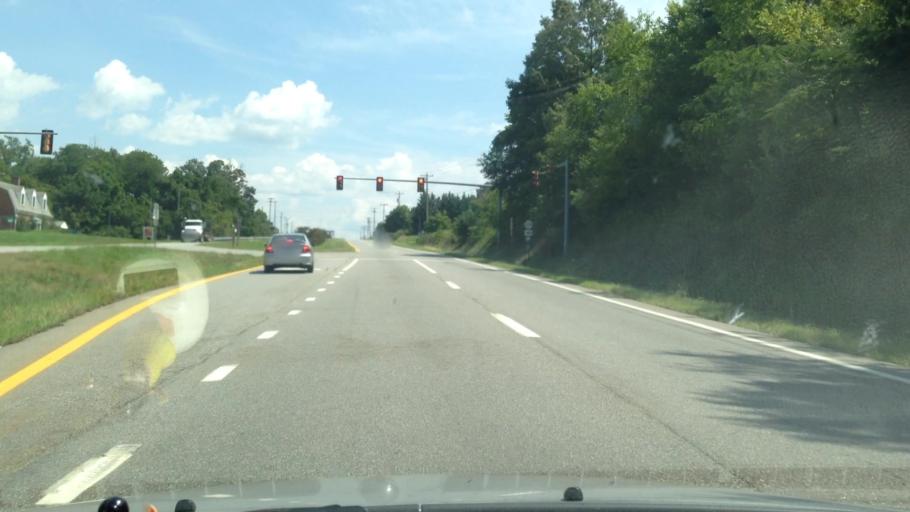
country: US
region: Virginia
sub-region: City of Martinsville
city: Martinsville
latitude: 36.6447
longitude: -79.8647
